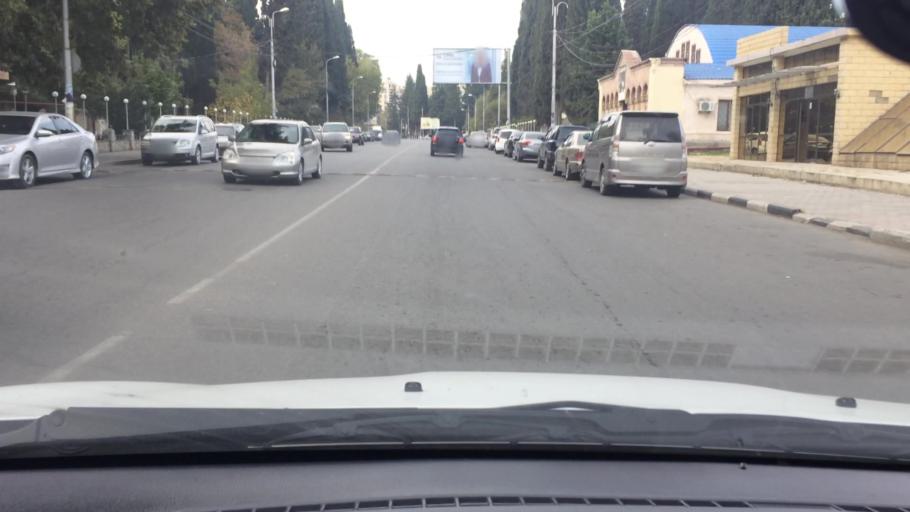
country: GE
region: Kvemo Kartli
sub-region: Marneuli
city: Marneuli
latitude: 41.4717
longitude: 44.8156
